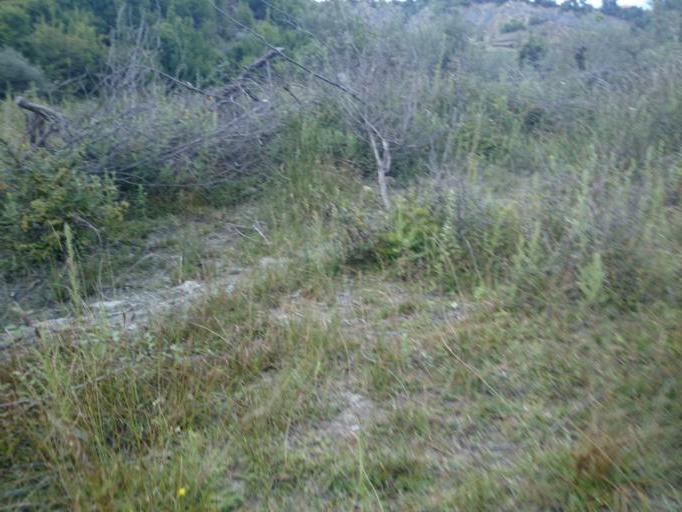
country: AL
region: Elbasan
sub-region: Rrethi i Gramshit
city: Porocan
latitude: 40.9360
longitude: 20.2702
